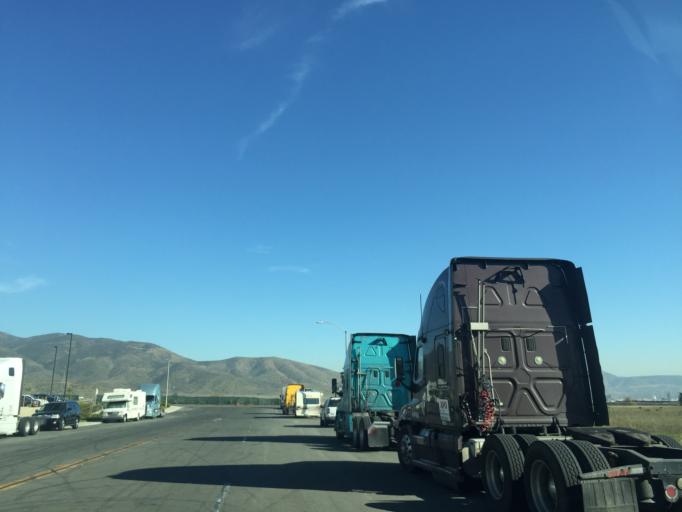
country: MX
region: Baja California
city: Tijuana
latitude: 32.5584
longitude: -116.9249
